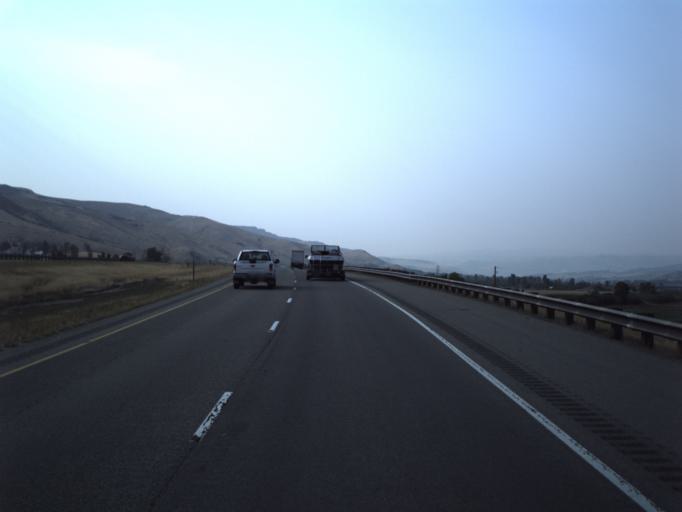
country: US
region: Utah
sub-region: Summit County
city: Coalville
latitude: 40.8458
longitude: -111.3878
